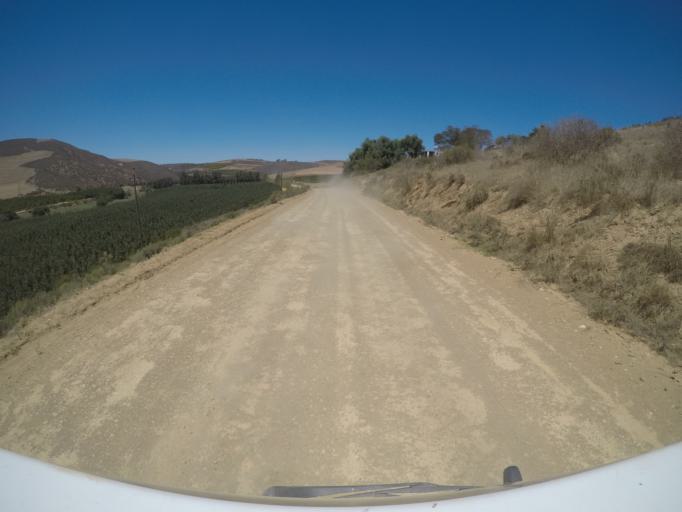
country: ZA
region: Western Cape
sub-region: Overberg District Municipality
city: Grabouw
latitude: -34.1073
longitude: 19.2108
